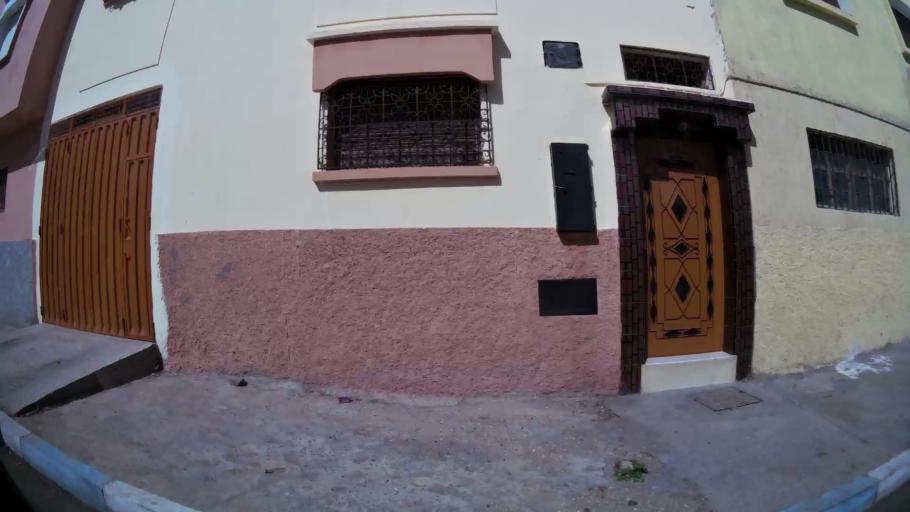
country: MA
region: Souss-Massa-Draa
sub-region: Inezgane-Ait Mellou
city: Inezgane
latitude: 30.3569
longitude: -9.5540
